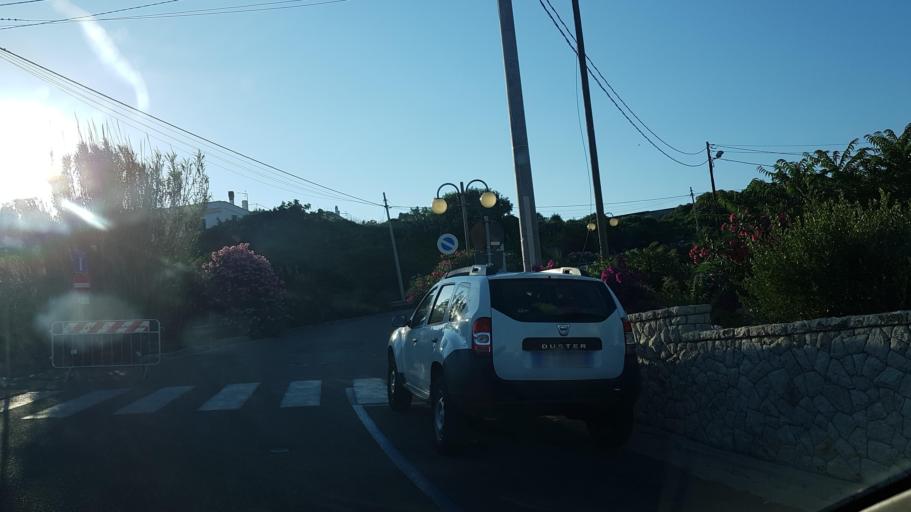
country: IT
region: Apulia
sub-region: Provincia di Lecce
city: Castro
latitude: 40.0013
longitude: 18.4229
